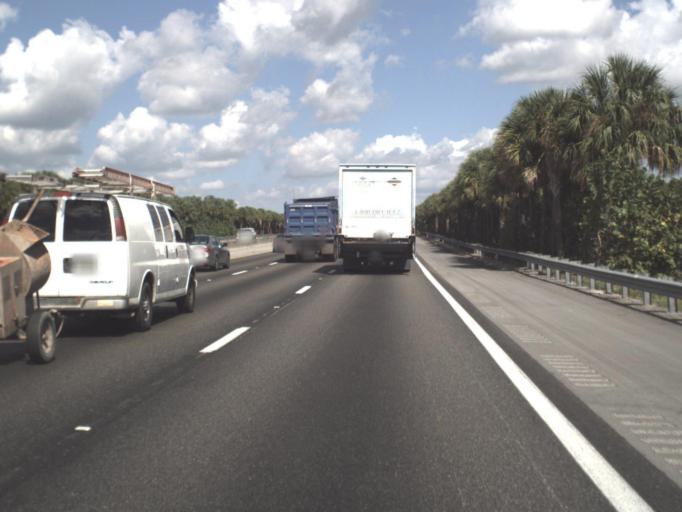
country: US
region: Florida
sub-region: Palm Beach County
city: Kings Point
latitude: 26.4045
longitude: -80.1712
